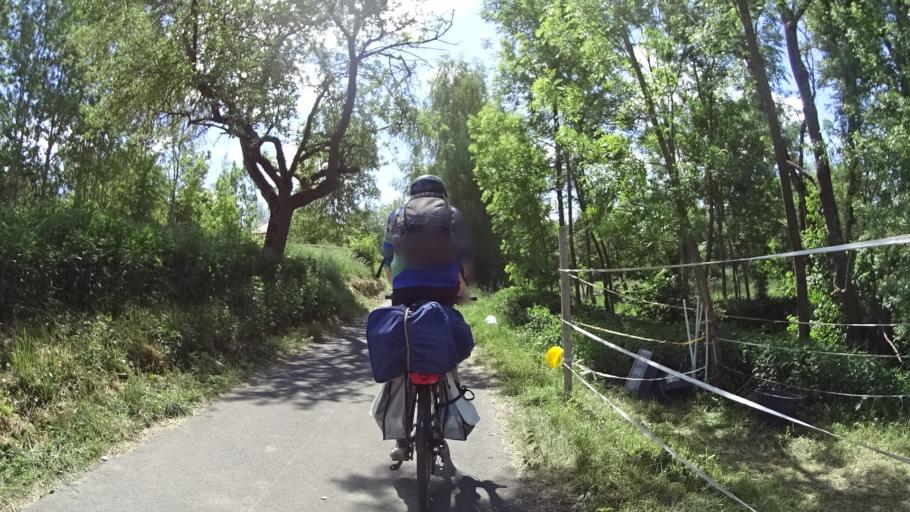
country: DE
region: Bavaria
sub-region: Regierungsbezirk Unterfranken
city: Bieberehren
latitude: 49.5053
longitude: 10.0189
